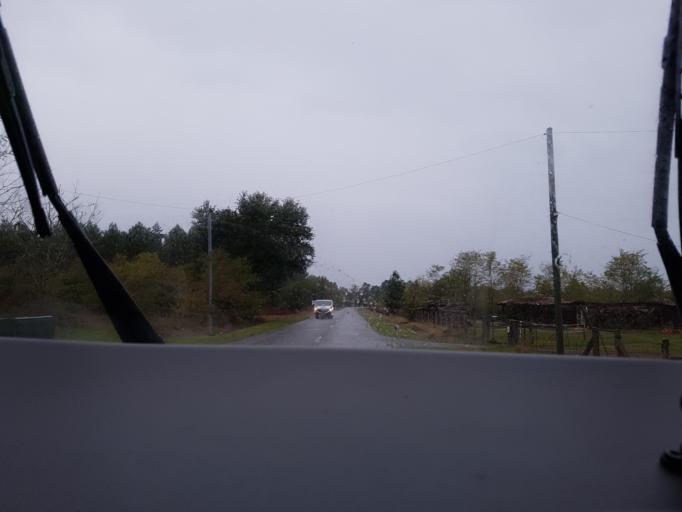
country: FR
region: Aquitaine
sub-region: Departement de la Gironde
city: Saint-Symphorien
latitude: 44.2655
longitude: -0.5601
